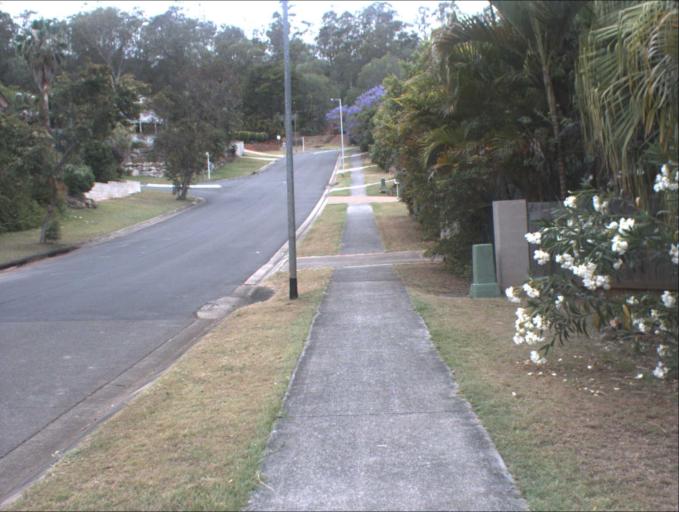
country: AU
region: Queensland
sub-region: Logan
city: Slacks Creek
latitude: -27.6739
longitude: 153.1689
